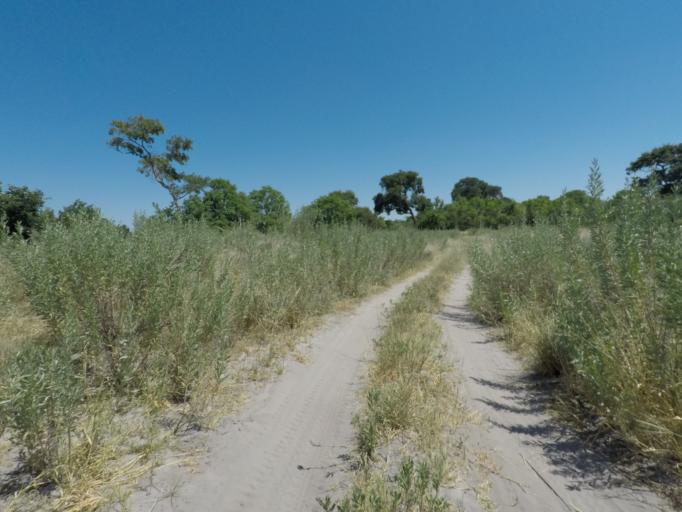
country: BW
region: North West
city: Maun
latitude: -19.4734
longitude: 23.5542
